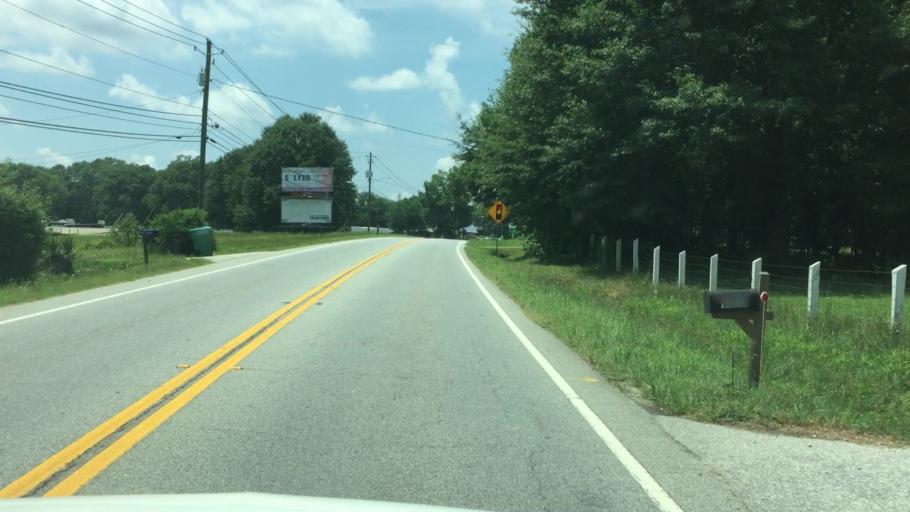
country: US
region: Georgia
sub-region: Barrow County
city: Auburn
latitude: 34.0037
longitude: -83.8084
